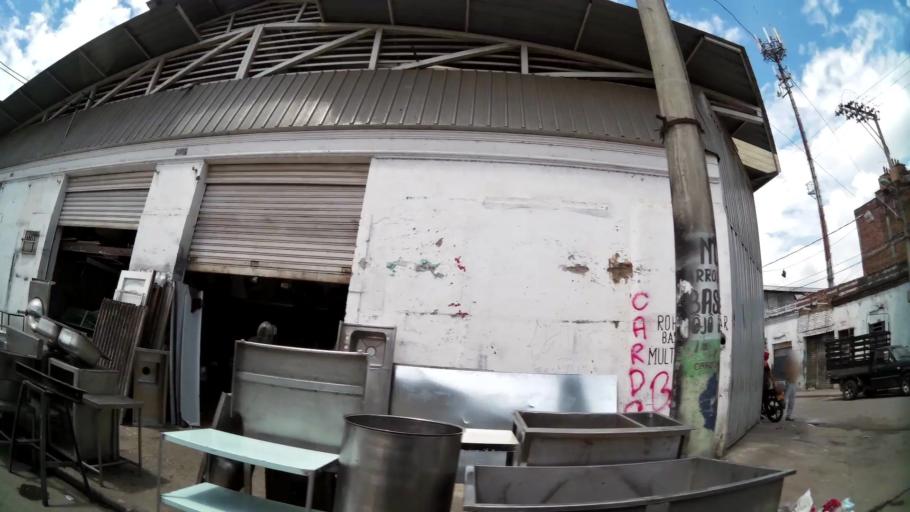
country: CO
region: Valle del Cauca
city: Cali
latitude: 3.4464
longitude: -76.5264
